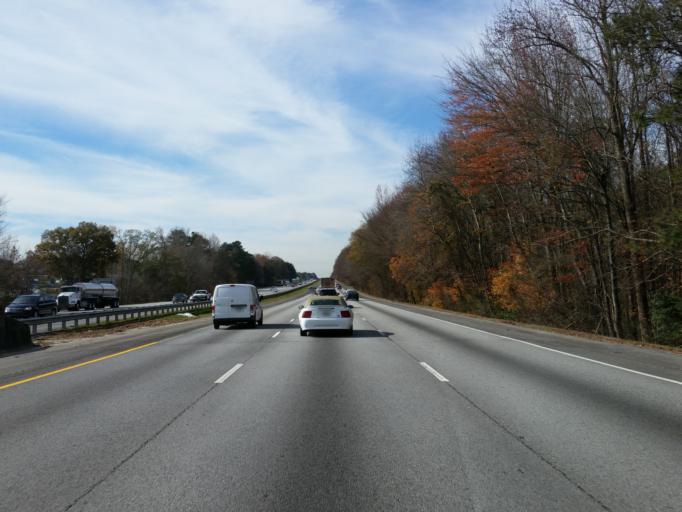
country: US
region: Georgia
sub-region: Cobb County
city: Austell
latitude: 33.7761
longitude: -84.6171
